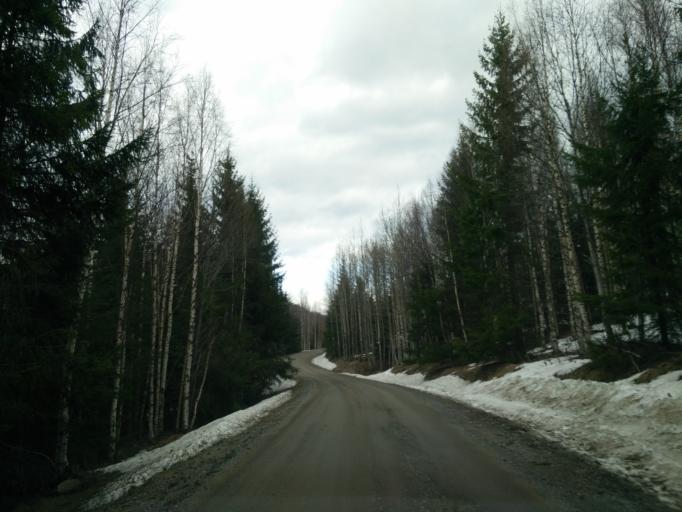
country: SE
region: Vaesternorrland
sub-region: Haernoesands Kommun
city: Haernoesand
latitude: 62.7295
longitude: 18.0259
